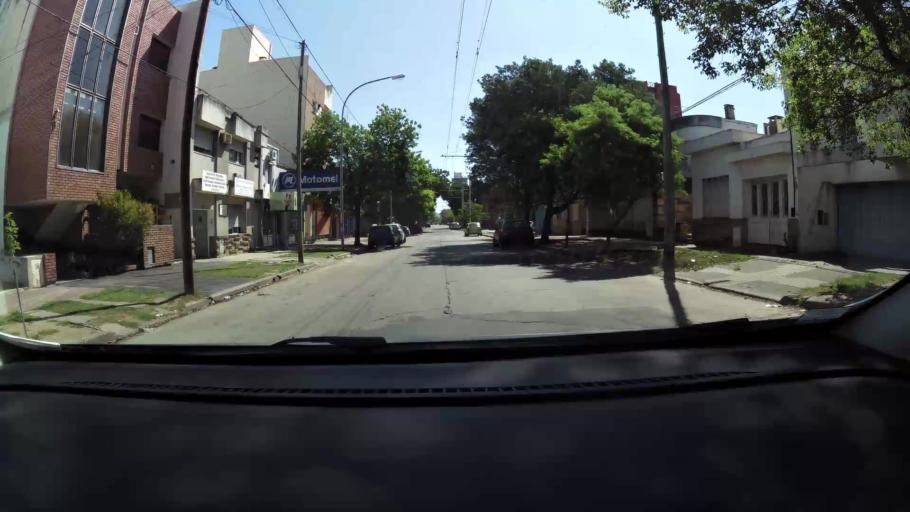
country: AR
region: Cordoba
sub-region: Departamento de Capital
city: Cordoba
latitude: -31.4095
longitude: -64.1631
